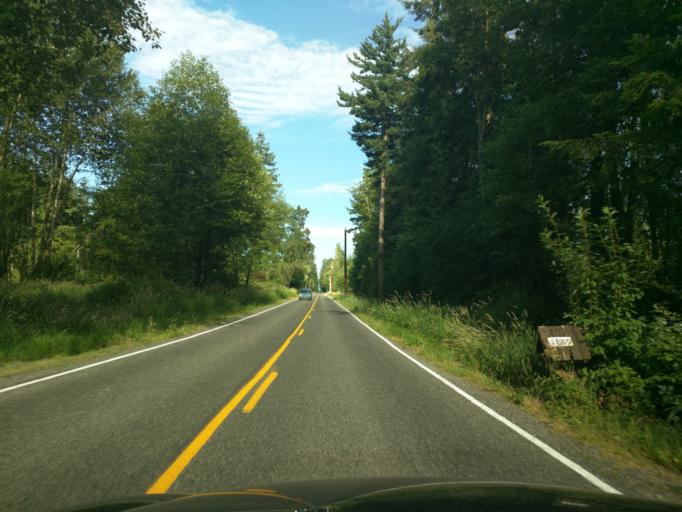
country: CA
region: British Columbia
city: Langley
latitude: 48.9934
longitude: -122.5843
